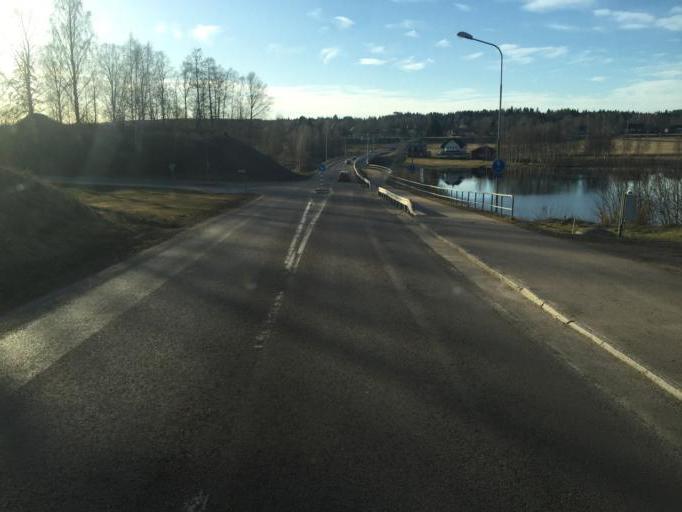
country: SE
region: Dalarna
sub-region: Gagnefs Kommun
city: Mockfjard
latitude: 60.5026
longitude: 14.9682
